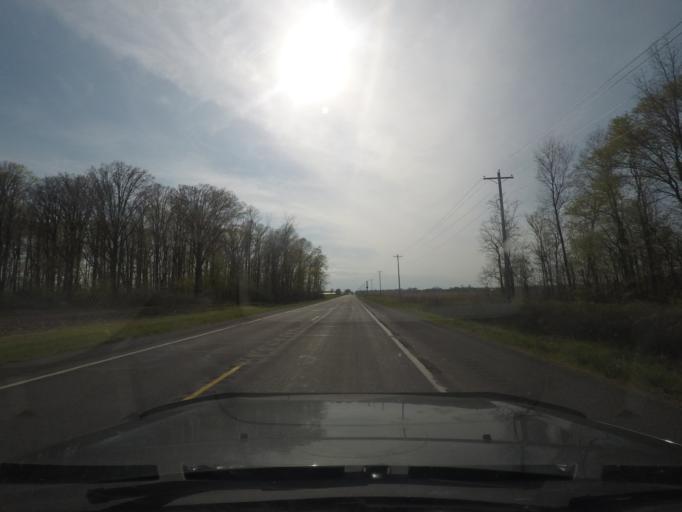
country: US
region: Michigan
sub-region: Berrien County
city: Three Oaks
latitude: 41.7982
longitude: -86.5372
